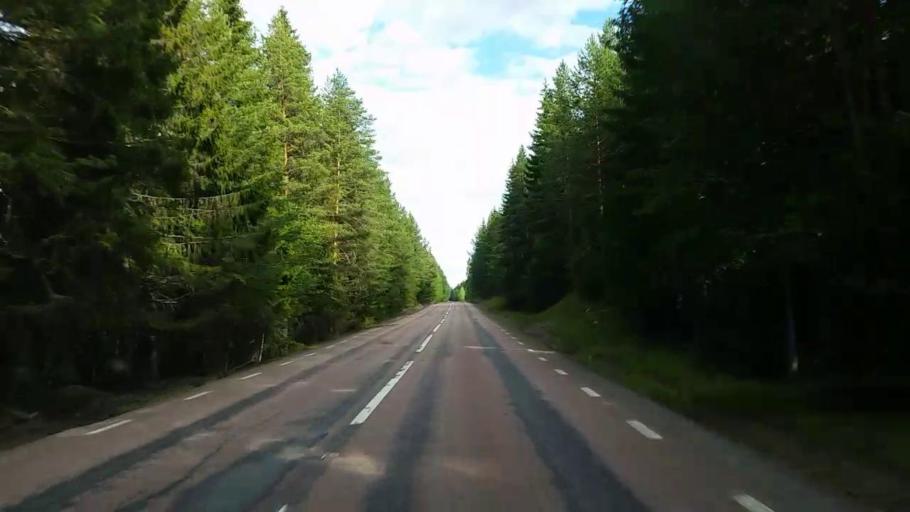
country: SE
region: Gaevleborg
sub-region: Ljusdals Kommun
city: Farila
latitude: 61.8827
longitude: 15.9393
